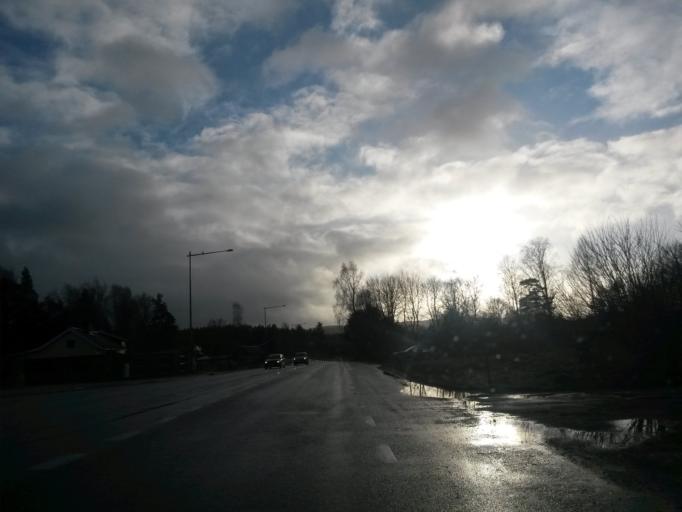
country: SE
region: Vaestra Goetaland
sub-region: Boras Kommun
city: Ganghester
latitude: 57.8129
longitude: 13.0123
